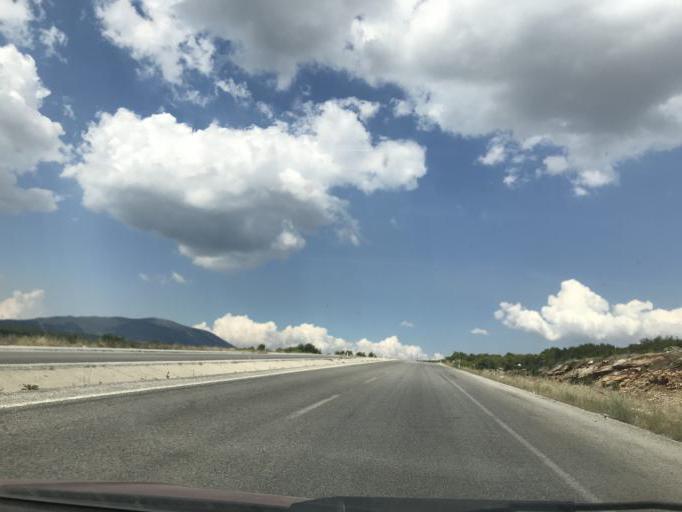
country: TR
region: Denizli
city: Tavas
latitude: 37.5873
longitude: 29.1044
